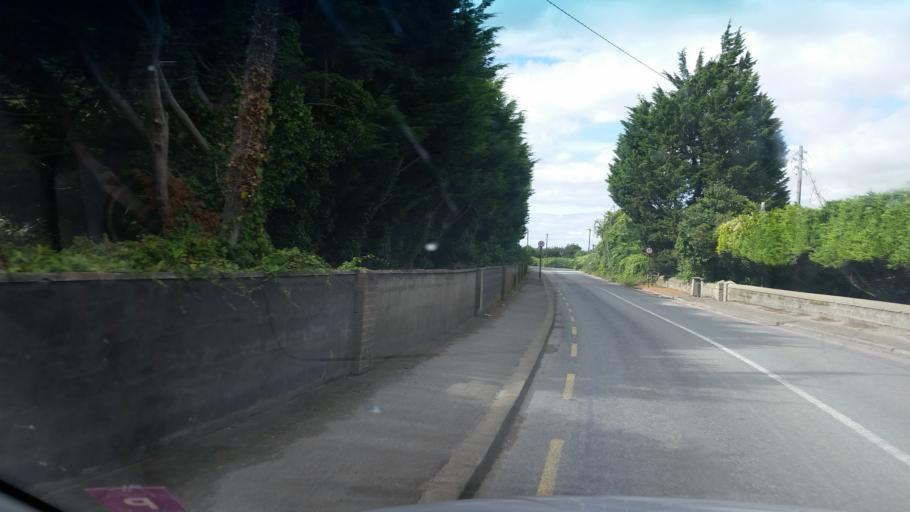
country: IE
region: Leinster
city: Kinsealy-Drinan
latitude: 53.4368
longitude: -6.1858
